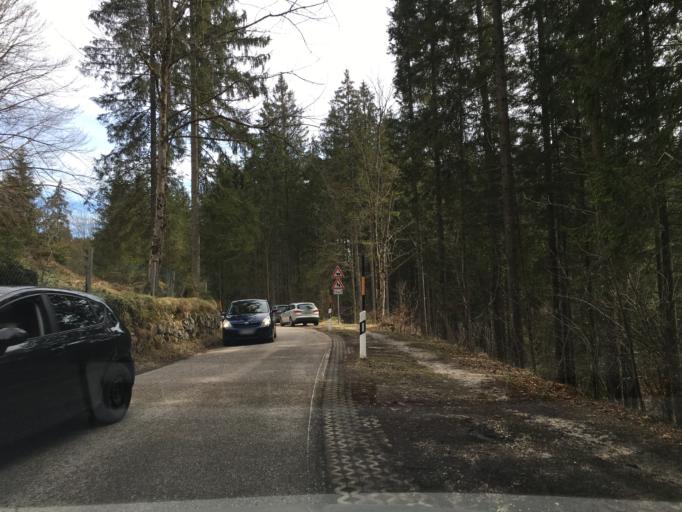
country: DE
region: Bavaria
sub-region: Upper Bavaria
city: Ramsau
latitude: 47.6091
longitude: 12.8557
